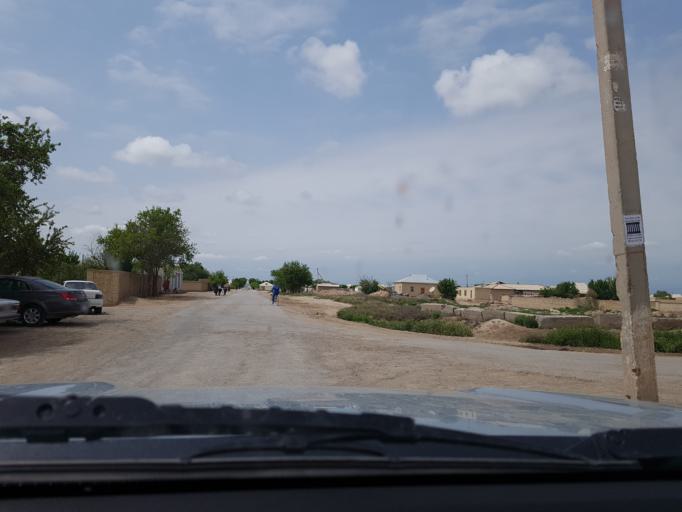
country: TM
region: Mary
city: Bayramaly
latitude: 37.6656
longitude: 62.1306
